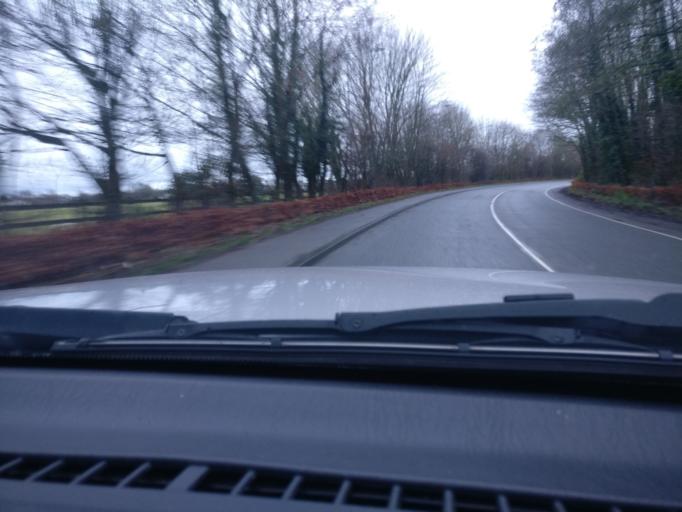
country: IE
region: Leinster
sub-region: An Mhi
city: Trim
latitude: 53.5564
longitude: -6.7818
